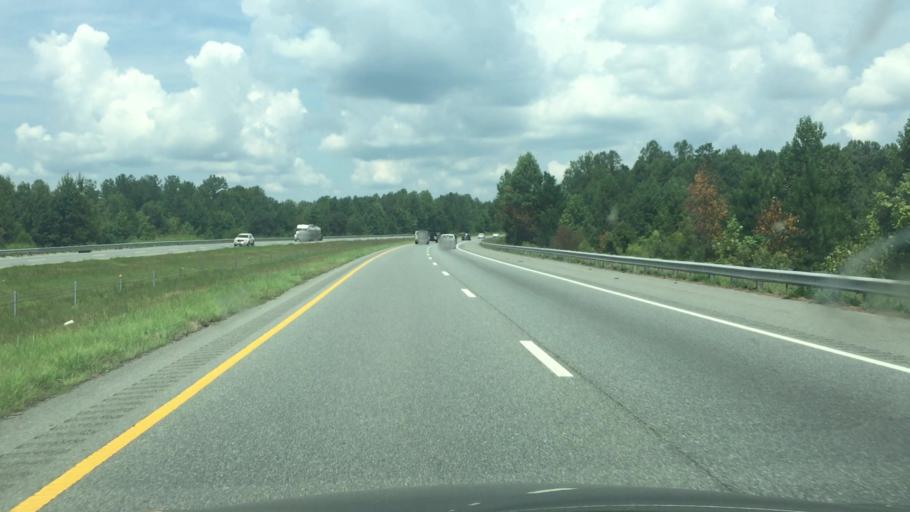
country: US
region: North Carolina
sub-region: Randolph County
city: Asheboro
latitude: 35.5608
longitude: -79.8032
